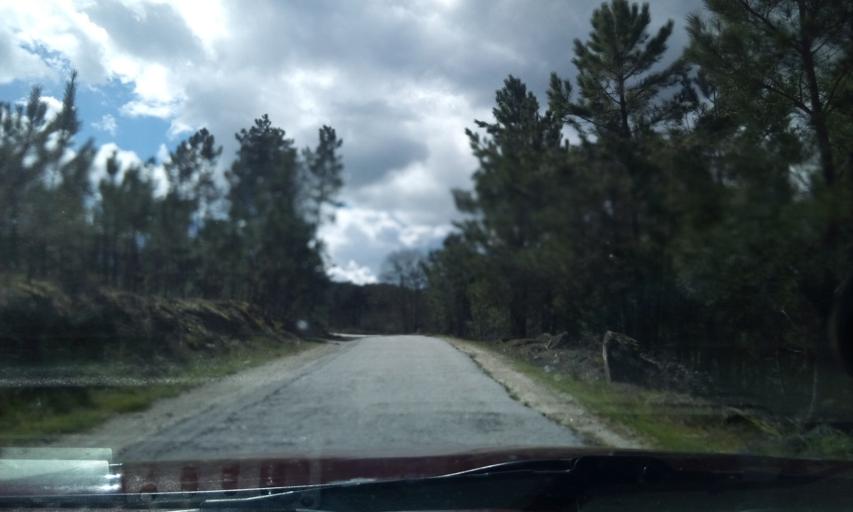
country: PT
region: Guarda
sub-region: Fornos de Algodres
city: Fornos de Algodres
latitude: 40.6554
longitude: -7.5108
